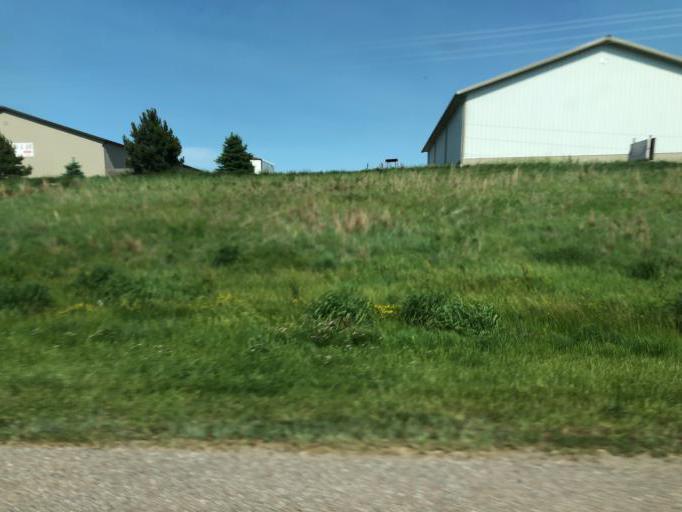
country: US
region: Nebraska
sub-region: York County
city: York
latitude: 40.7431
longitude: -97.6049
